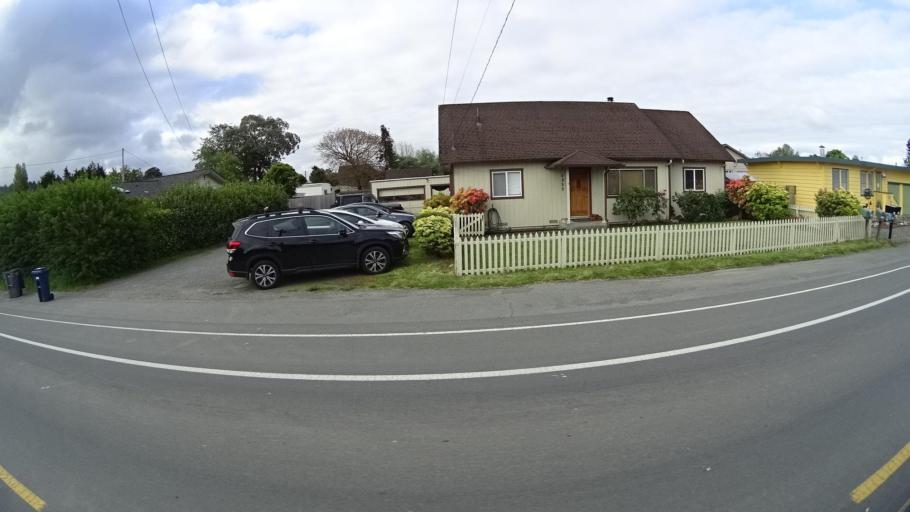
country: US
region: California
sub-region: Humboldt County
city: Arcata
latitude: 40.8897
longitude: -124.0856
